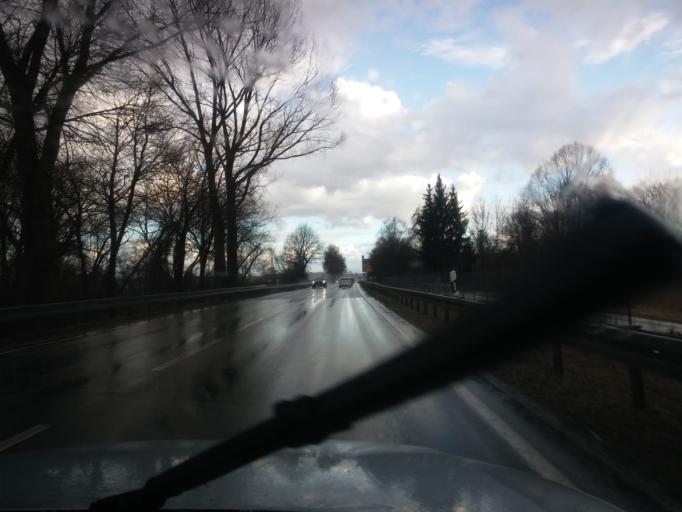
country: DE
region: Bavaria
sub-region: Upper Bavaria
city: Ismaning
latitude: 48.2048
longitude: 11.7004
